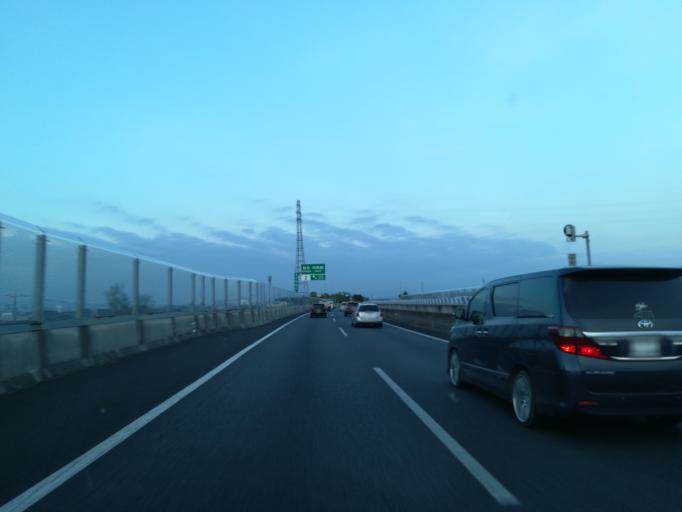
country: JP
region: Gunma
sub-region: Sawa-gun
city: Tamamura
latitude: 36.3447
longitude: 139.1396
